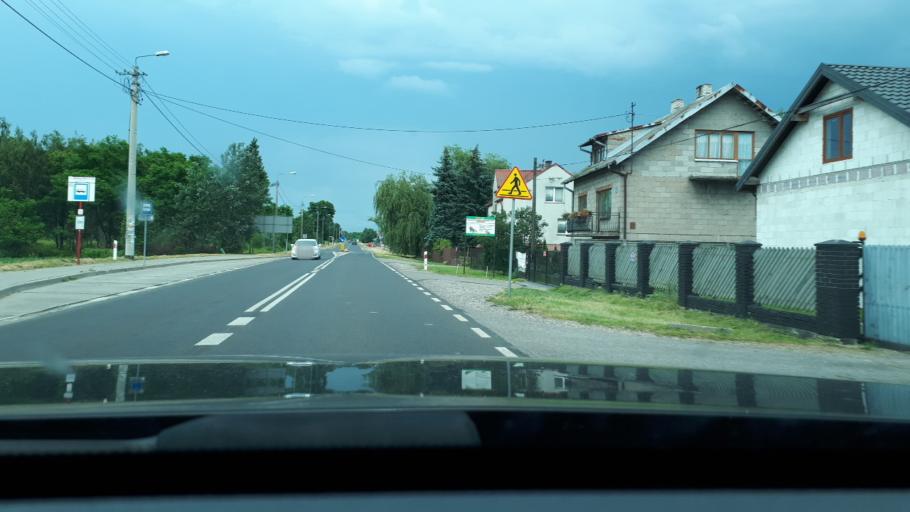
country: PL
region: Masovian Voivodeship
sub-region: Powiat warszawski zachodni
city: Kampinos
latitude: 52.2590
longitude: 20.5250
